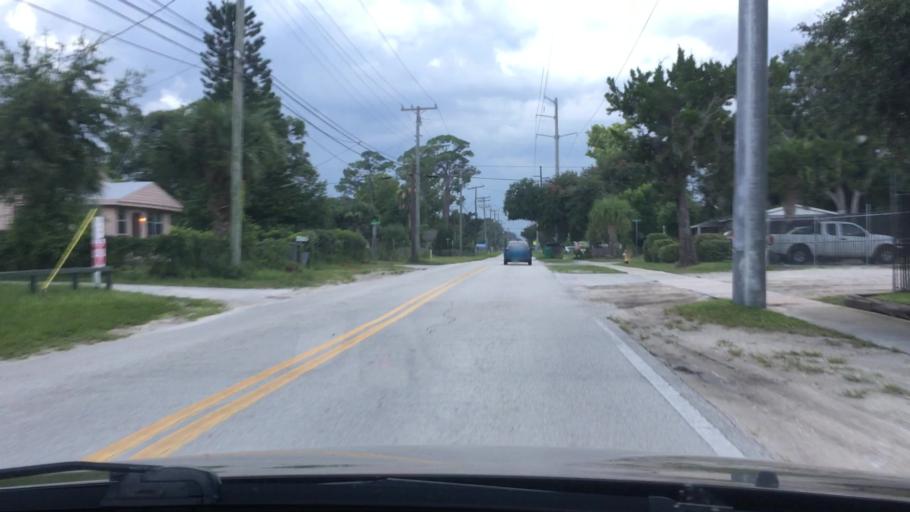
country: US
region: Florida
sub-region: Volusia County
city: Holly Hill
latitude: 29.2467
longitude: -81.0493
